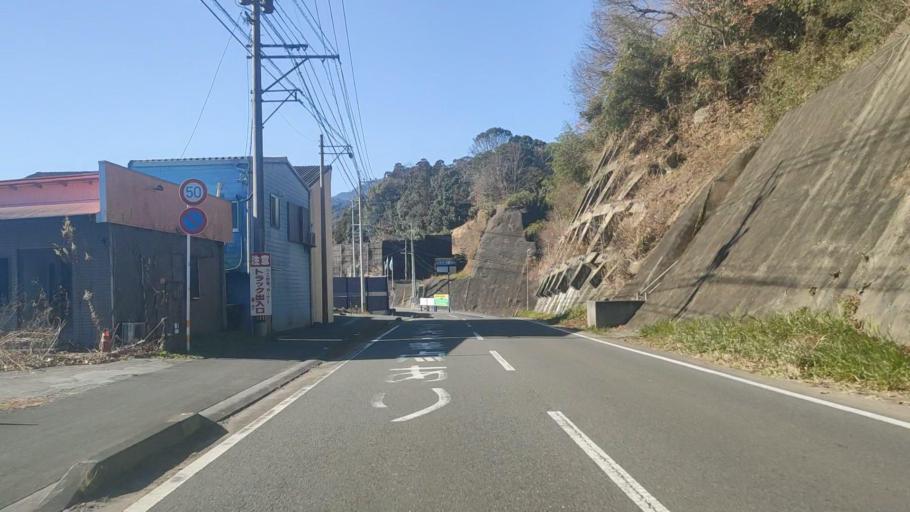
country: JP
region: Oita
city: Saiki
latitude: 32.9759
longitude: 131.8546
